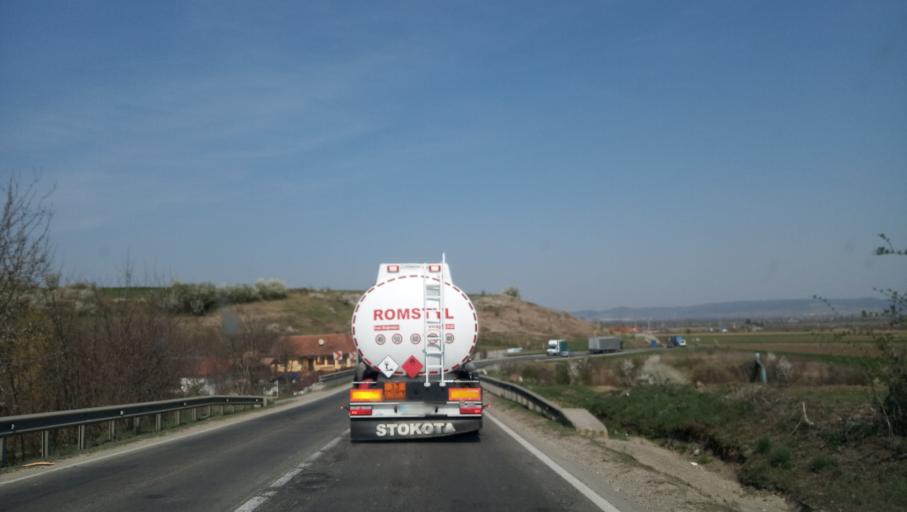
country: RO
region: Alba
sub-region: Comuna Radesti
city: Radesti
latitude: 46.2492
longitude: 23.6879
